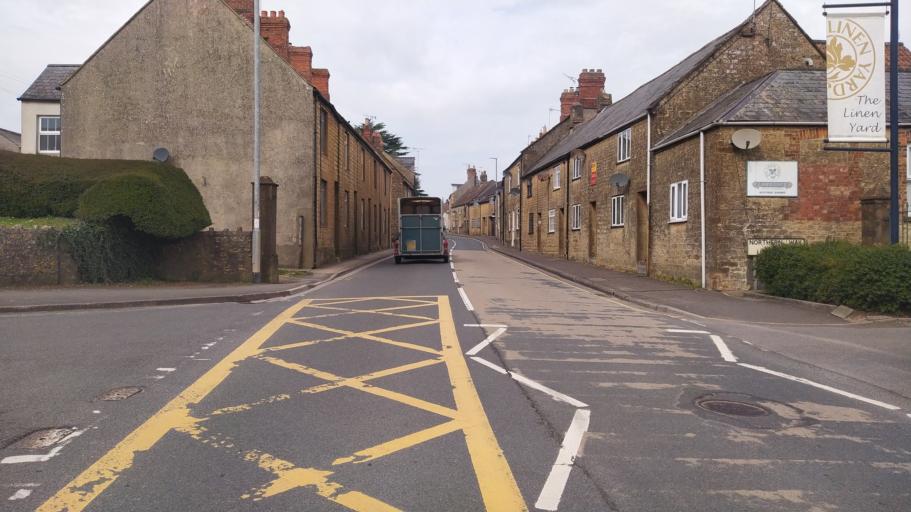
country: GB
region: England
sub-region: Somerset
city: Crewkerne
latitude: 50.8819
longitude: -2.7918
